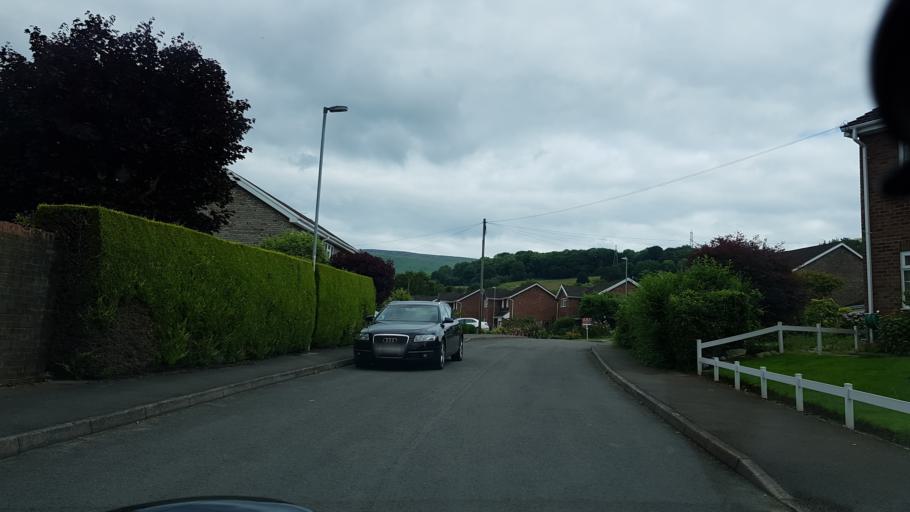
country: GB
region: Wales
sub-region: Monmouthshire
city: Gilwern
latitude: 51.8272
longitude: -3.1004
